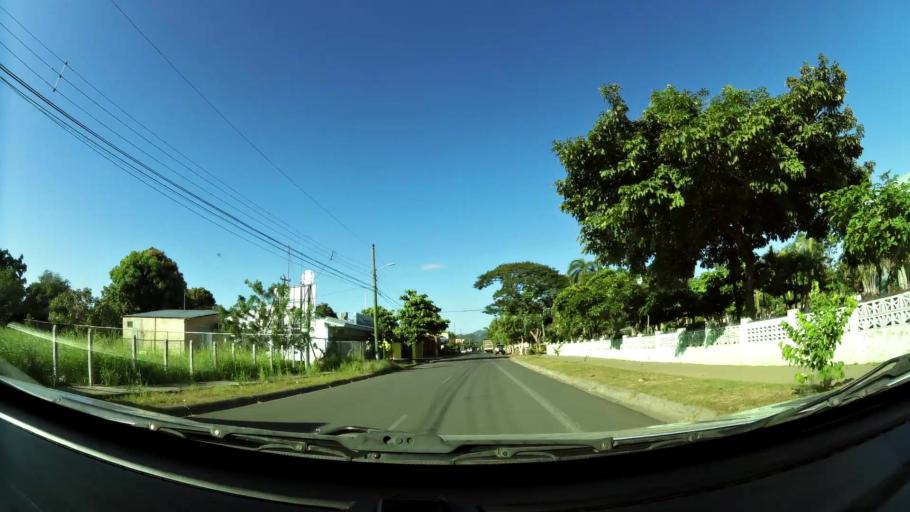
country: CR
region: Guanacaste
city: Belen
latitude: 10.4449
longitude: -85.5497
